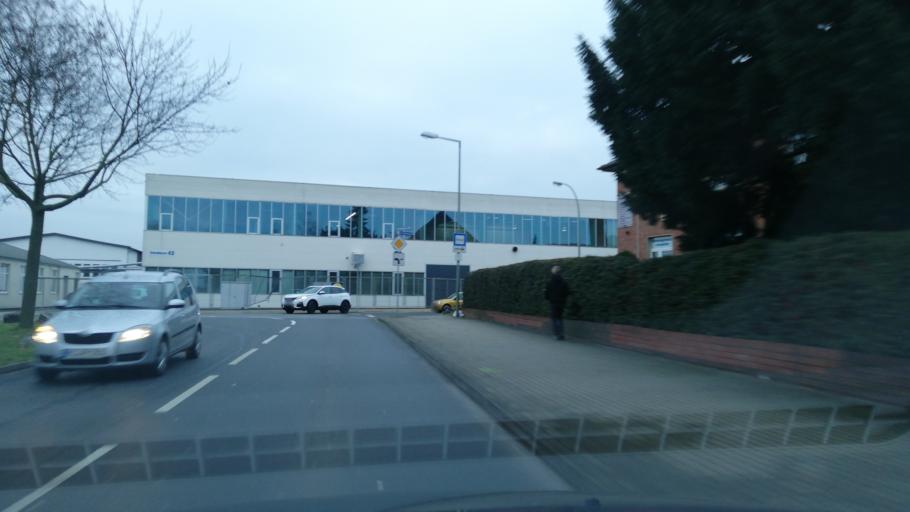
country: DE
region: Hesse
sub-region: Regierungsbezirk Kassel
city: Lohfelden
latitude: 51.2974
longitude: 9.5342
